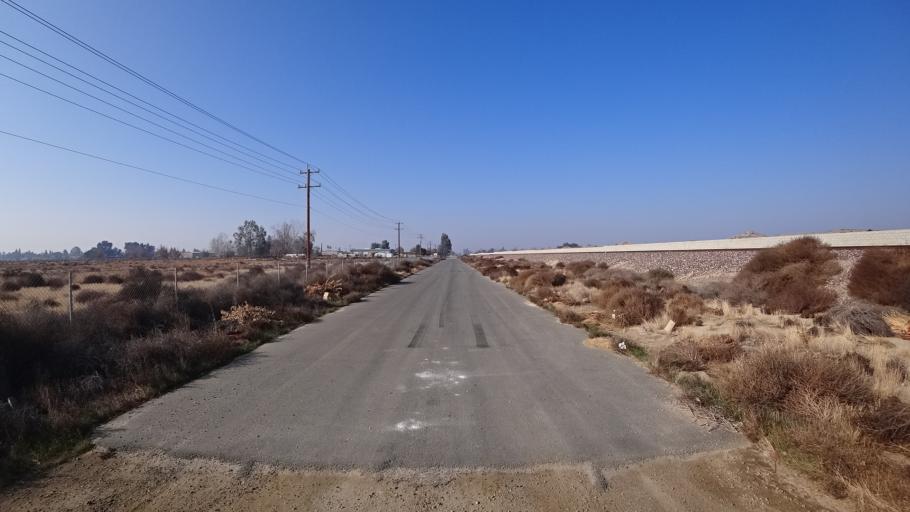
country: US
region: California
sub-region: Kern County
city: Greenacres
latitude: 35.3761
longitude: -119.1014
